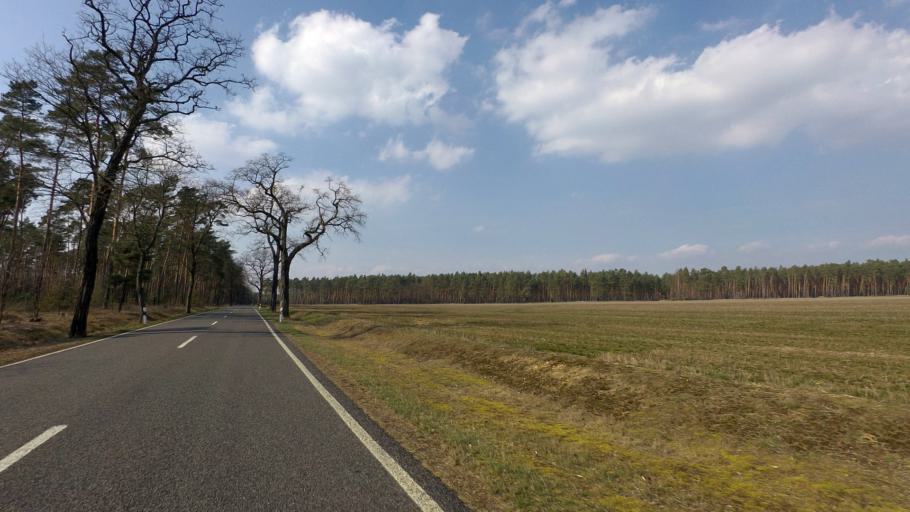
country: DE
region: Brandenburg
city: Dahme
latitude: 51.9228
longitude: 13.4721
